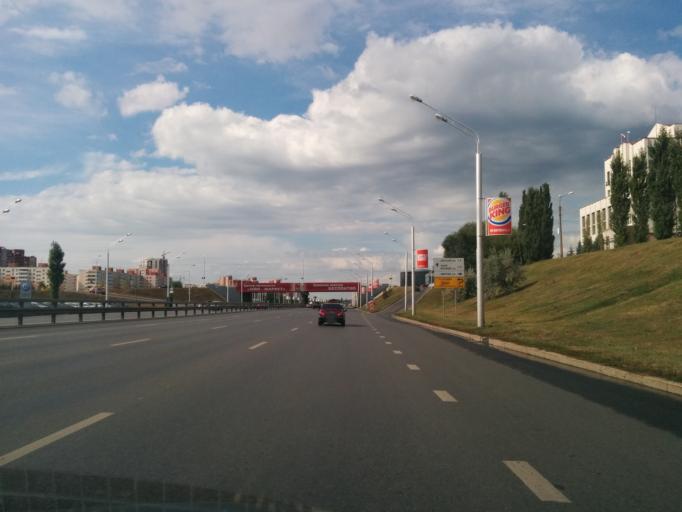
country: RU
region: Bashkortostan
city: Ufa
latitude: 54.7265
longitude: 55.9903
